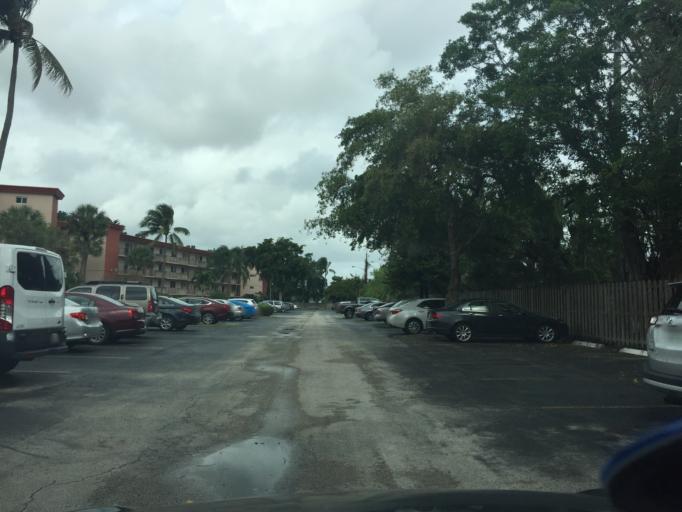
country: US
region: Florida
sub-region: Broward County
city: Plantation
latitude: 26.1370
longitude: -80.2264
